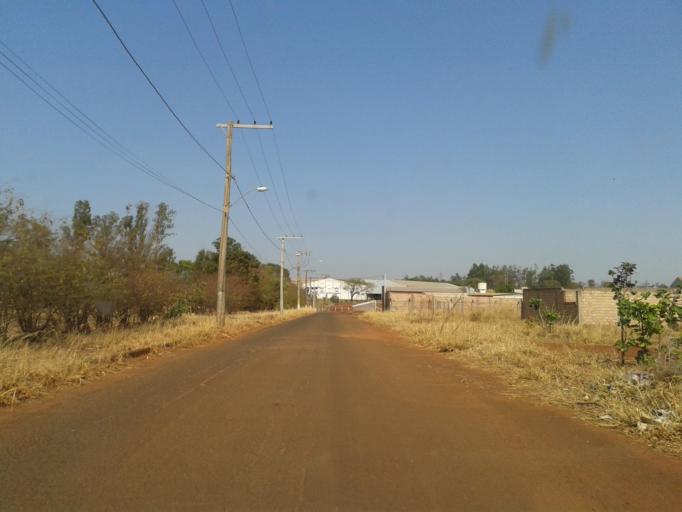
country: BR
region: Minas Gerais
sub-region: Ituiutaba
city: Ituiutaba
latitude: -18.9618
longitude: -49.4893
